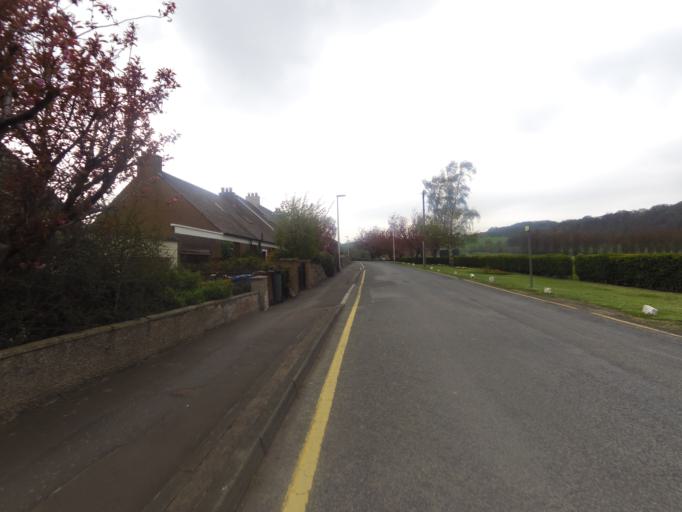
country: GB
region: Scotland
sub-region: Fife
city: Aberdour
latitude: 56.0537
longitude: -3.2924
